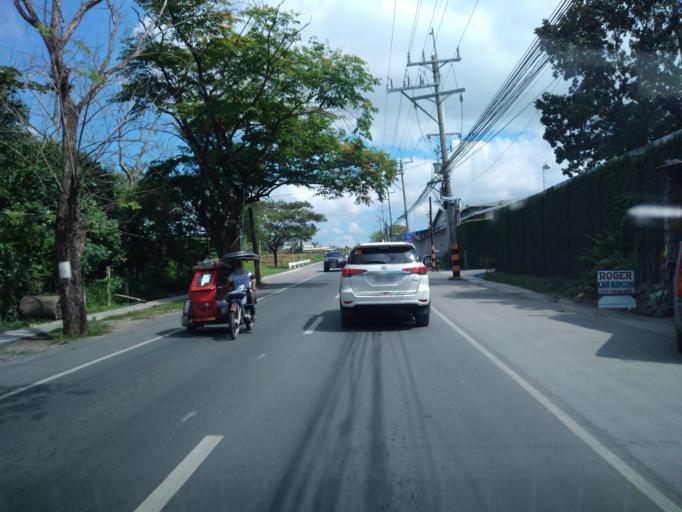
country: PH
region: Central Luzon
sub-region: Province of Bulacan
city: Santa Maria
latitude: 14.8271
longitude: 120.9705
